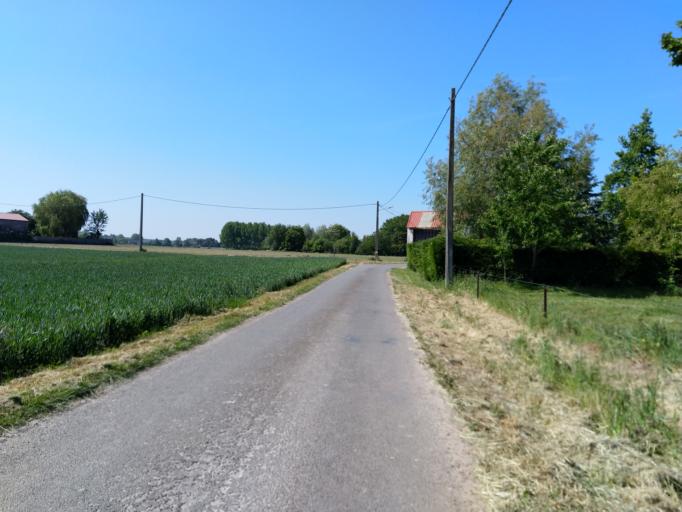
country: BE
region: Wallonia
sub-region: Province du Hainaut
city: Lens
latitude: 50.5391
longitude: 3.8647
